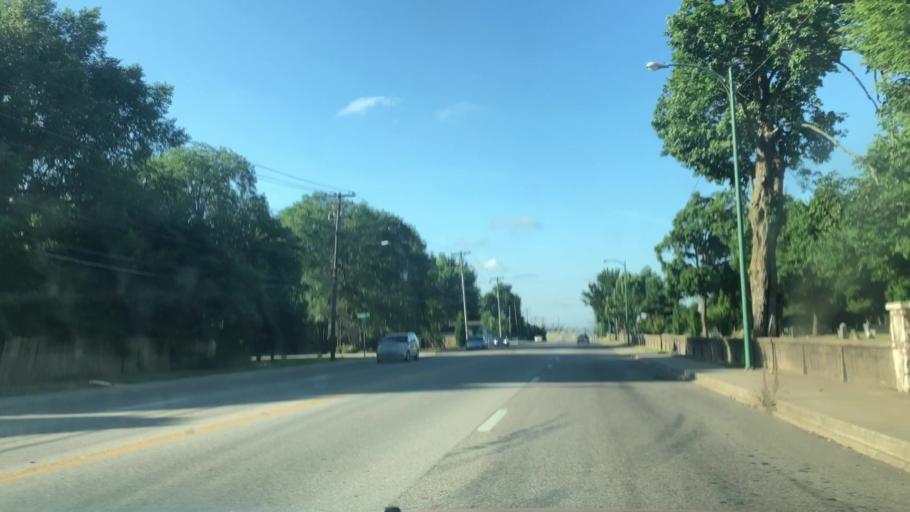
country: US
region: Missouri
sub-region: Greene County
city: Springfield
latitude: 37.1719
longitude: -93.2626
